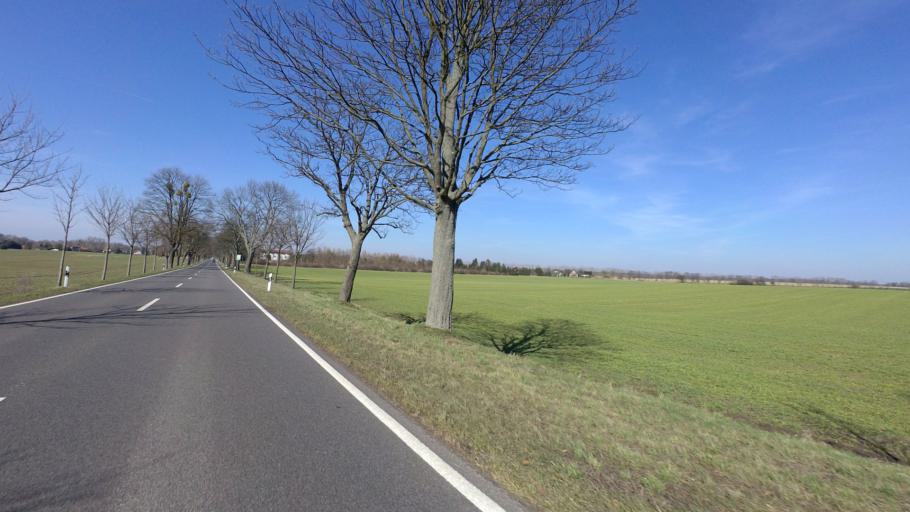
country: DE
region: Brandenburg
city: Eberswalde
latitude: 52.7656
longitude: 13.8396
